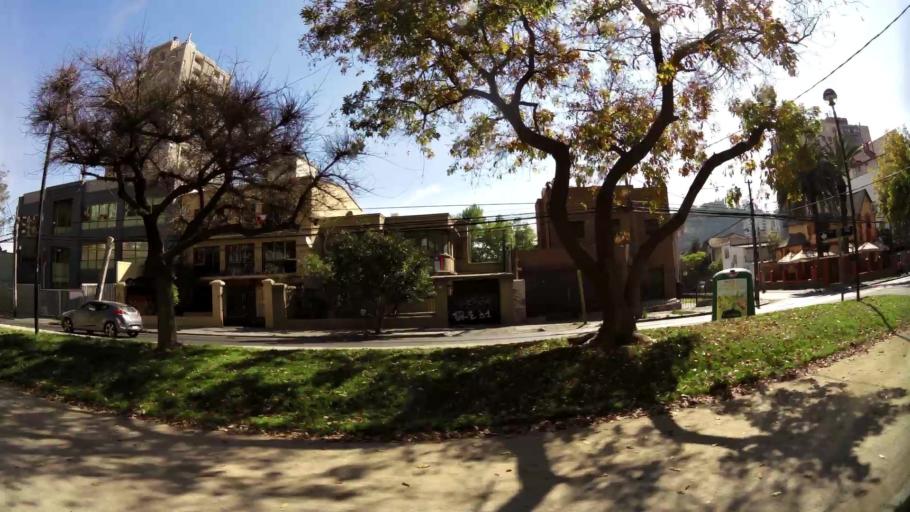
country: CL
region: Santiago Metropolitan
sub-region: Provincia de Santiago
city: Santiago
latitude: -33.4219
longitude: -70.6404
